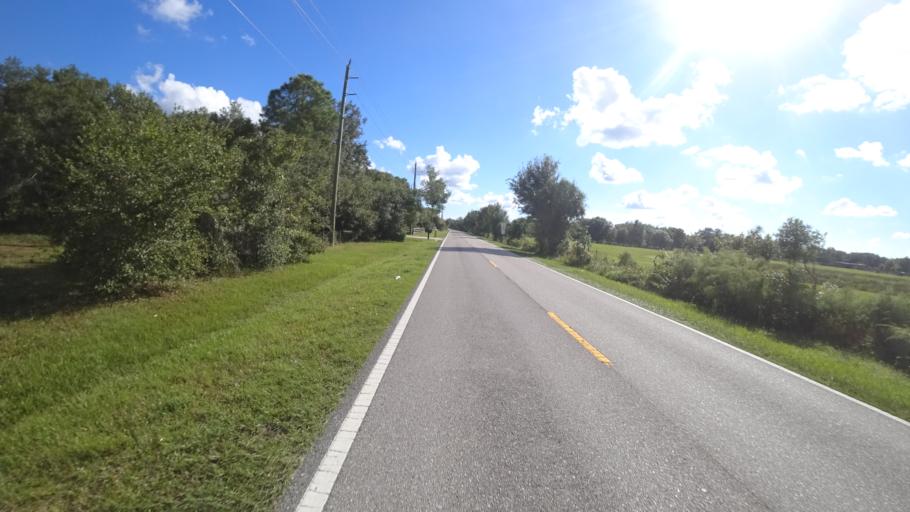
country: US
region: Florida
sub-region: Sarasota County
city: Lake Sarasota
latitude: 27.3318
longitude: -82.2694
